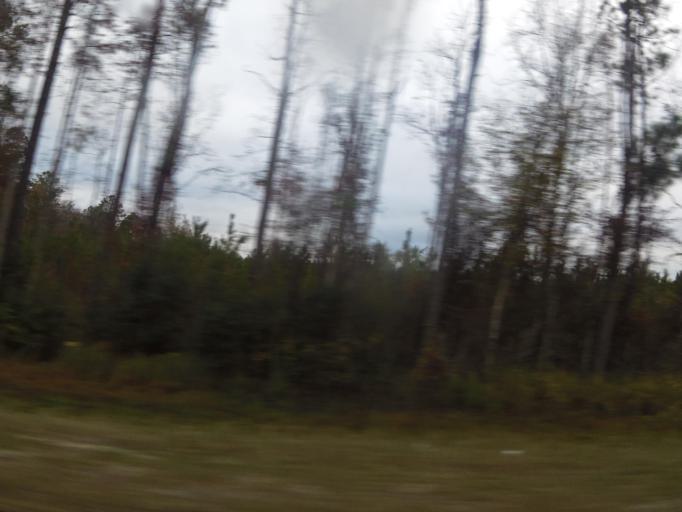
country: US
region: Georgia
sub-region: Charlton County
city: Folkston
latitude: 30.8826
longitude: -82.0380
